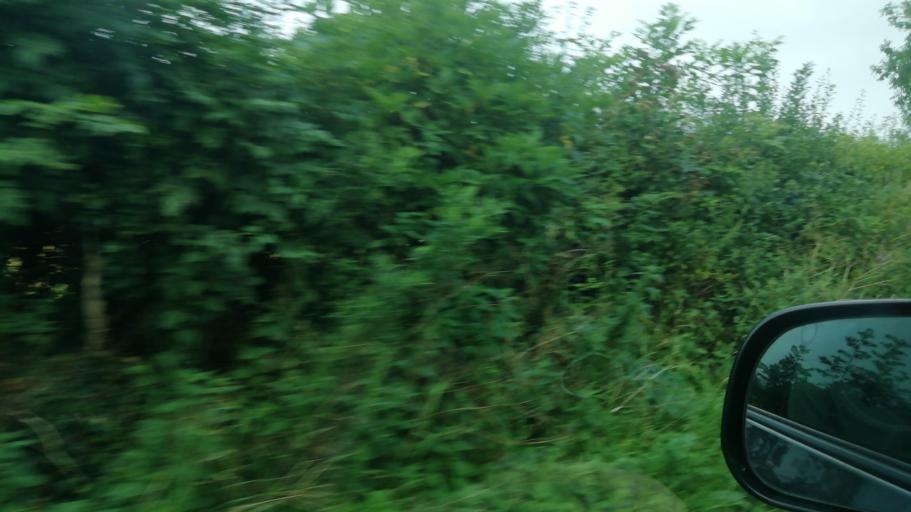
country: IE
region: Munster
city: Fethard
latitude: 52.5715
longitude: -7.5834
